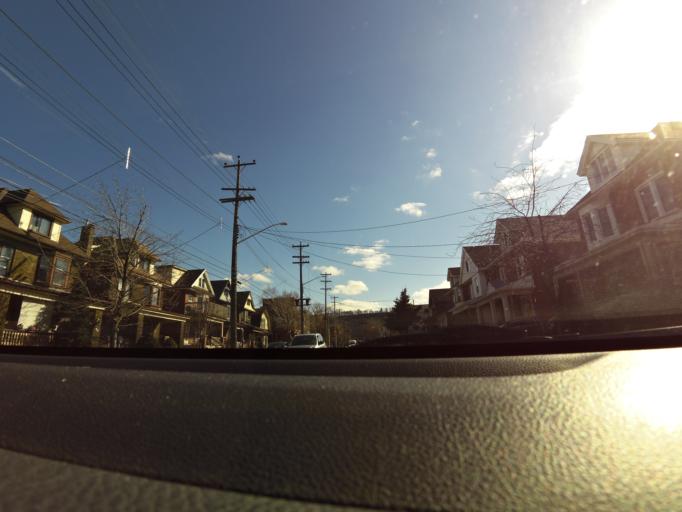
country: CA
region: Ontario
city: Hamilton
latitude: 43.2460
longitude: -79.8300
